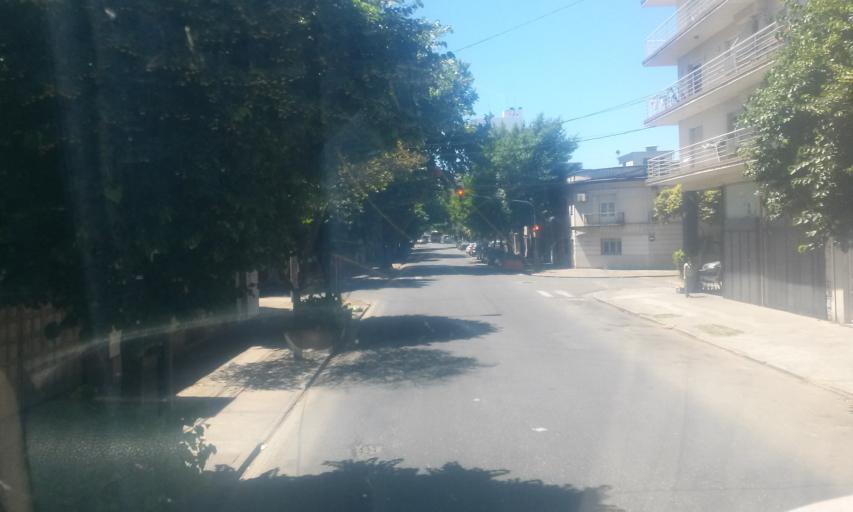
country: AR
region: Santa Fe
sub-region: Departamento de Rosario
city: Rosario
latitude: -32.9391
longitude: -60.6782
